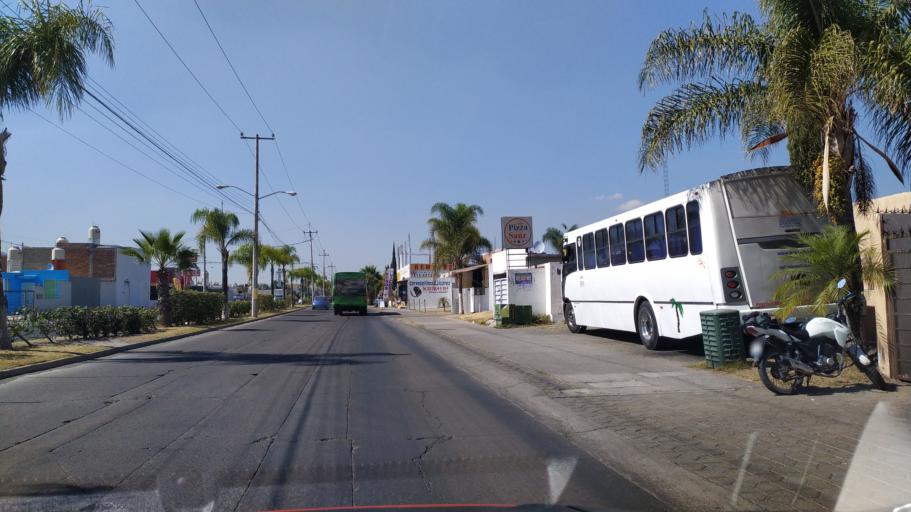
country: MX
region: Jalisco
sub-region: Tlajomulco de Zuniga
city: Villas de la Hacienda [Fraccionamiento]
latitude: 20.5296
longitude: -103.3923
